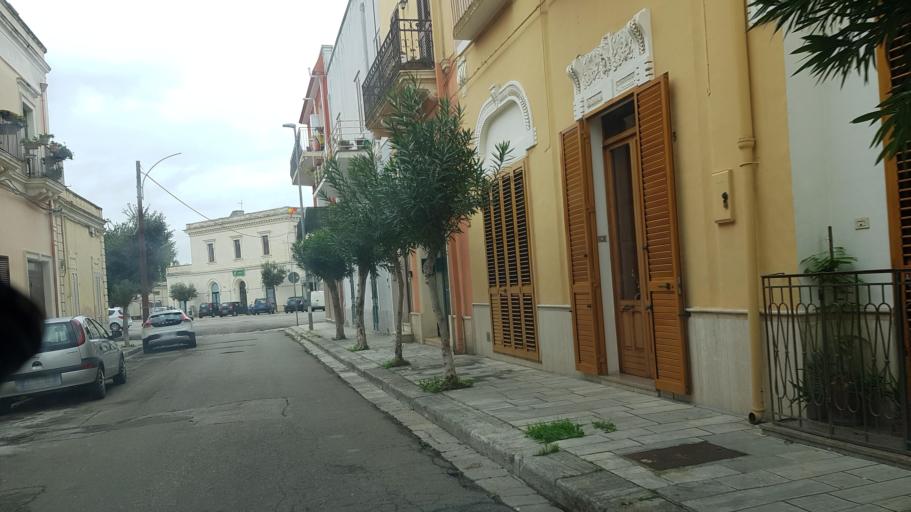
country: IT
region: Apulia
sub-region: Provincia di Lecce
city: Novoli
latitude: 40.3805
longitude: 18.0488
